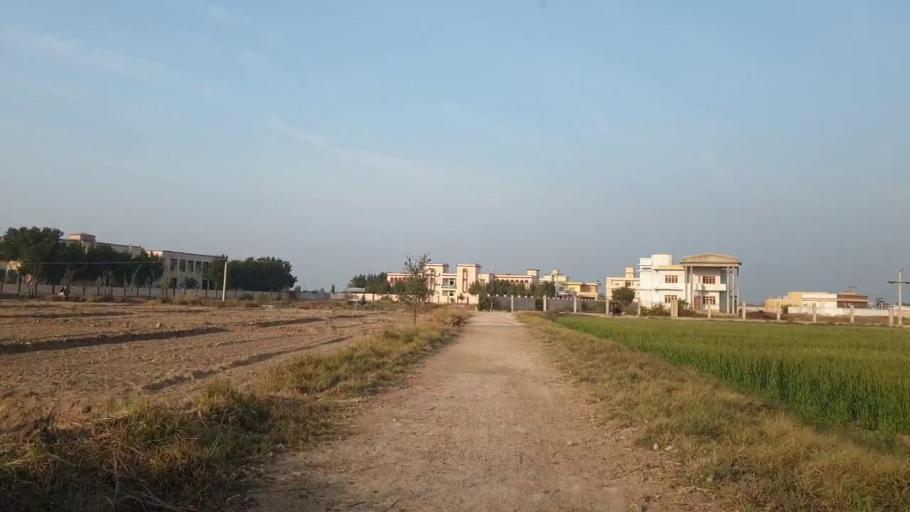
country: PK
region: Sindh
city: Matiari
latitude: 25.6029
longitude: 68.4369
